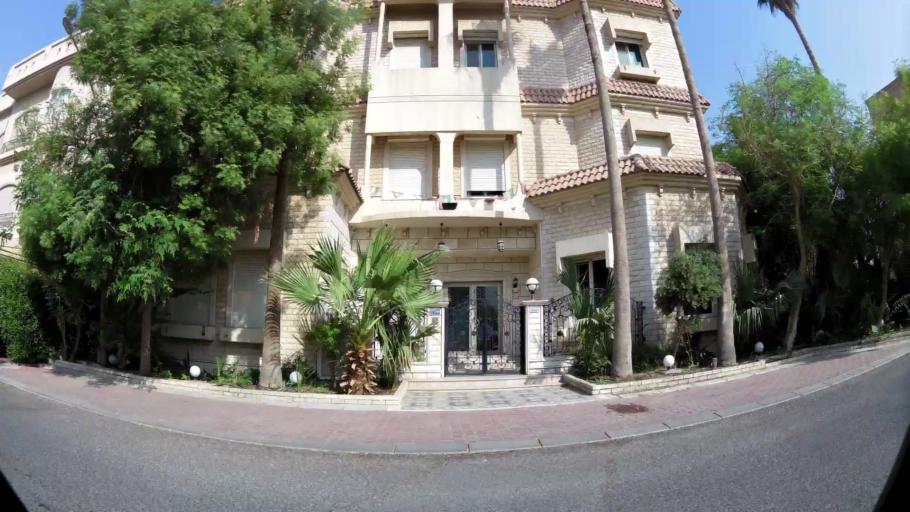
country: KW
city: Bayan
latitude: 29.2868
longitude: 48.0504
